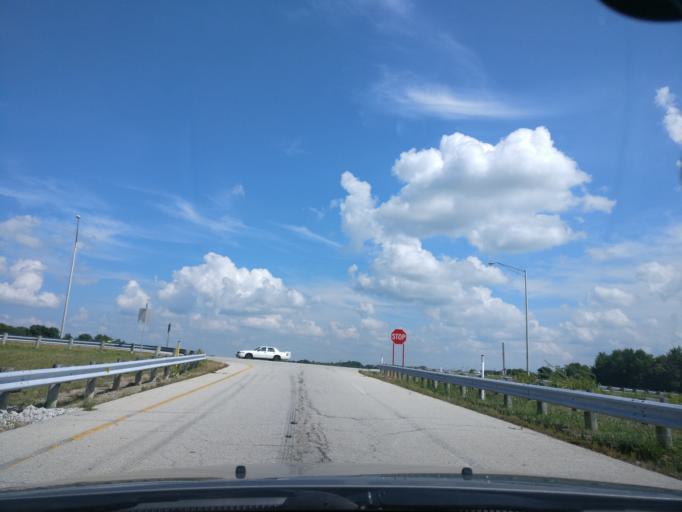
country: US
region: Ohio
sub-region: Greene County
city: Jamestown
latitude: 39.6697
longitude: -83.7370
